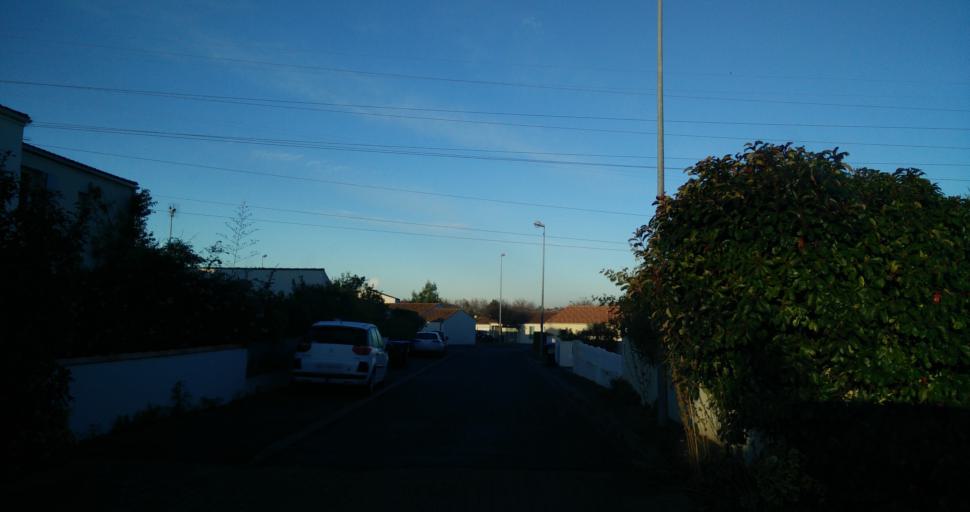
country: FR
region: Poitou-Charentes
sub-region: Departement de la Charente-Maritime
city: Puilboreau
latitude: 46.1866
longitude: -1.1233
